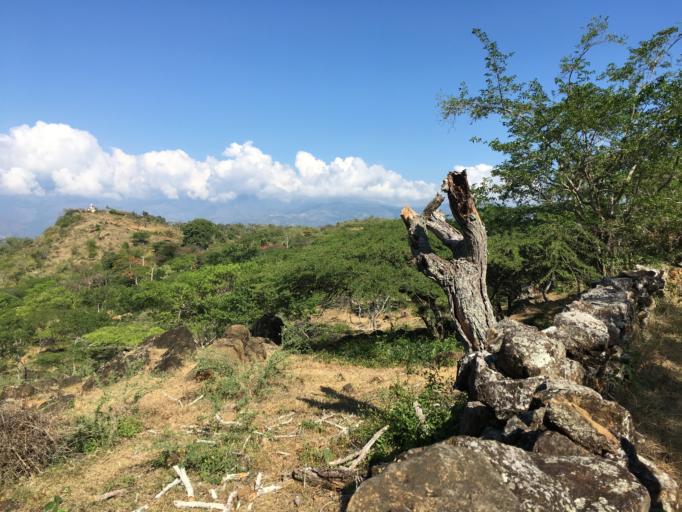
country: CO
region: Santander
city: Barichara
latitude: 6.6662
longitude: -73.2325
